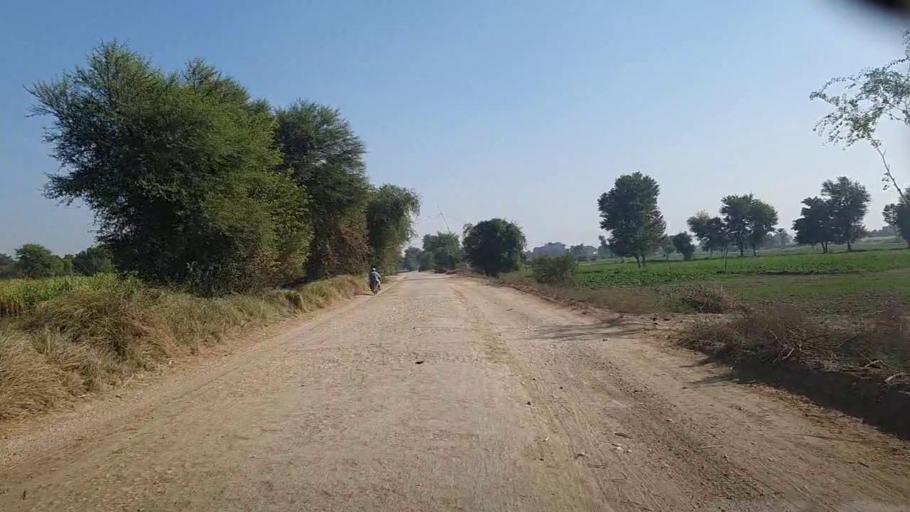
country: PK
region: Sindh
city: Darya Khan Marri
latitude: 26.6629
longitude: 68.3403
